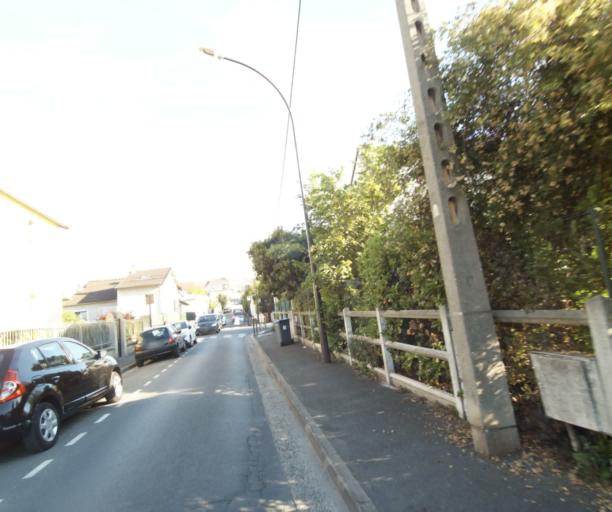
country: FR
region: Ile-de-France
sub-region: Departement du Val-d'Oise
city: Argenteuil
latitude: 48.9376
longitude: 2.2318
